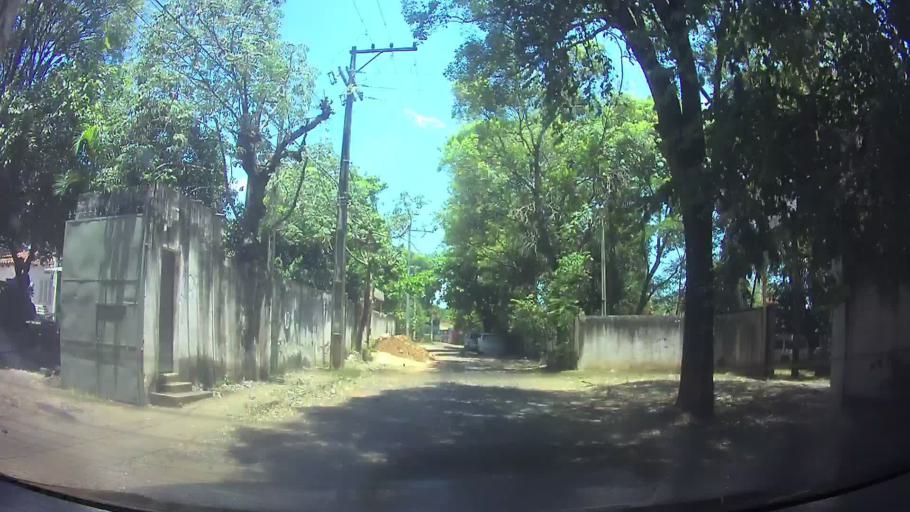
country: PY
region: Central
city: Lambare
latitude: -25.3120
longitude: -57.5955
